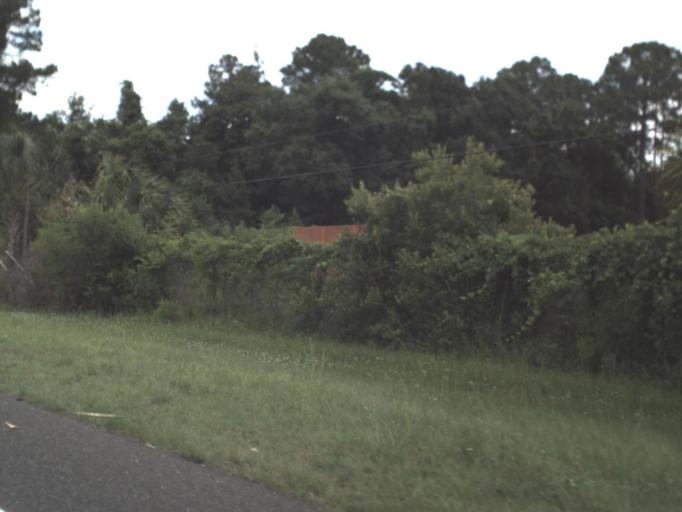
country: US
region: Florida
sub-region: Nassau County
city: Hilliard
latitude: 30.7090
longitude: -81.9301
